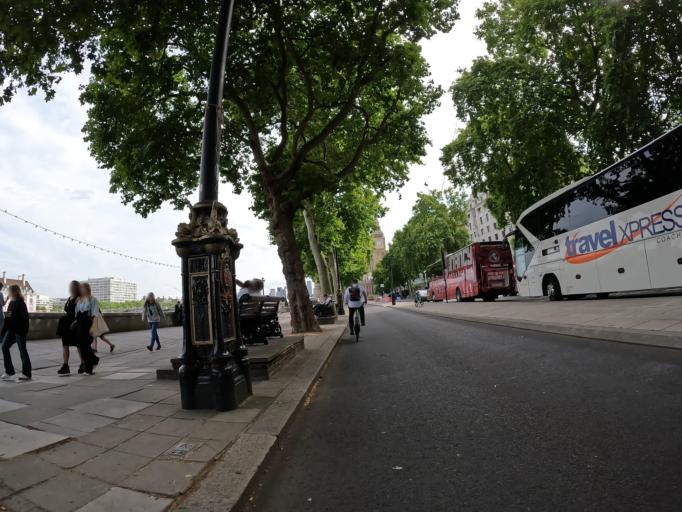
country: GB
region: England
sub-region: Greater London
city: Bromley
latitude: 51.4112
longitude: 0.0223
